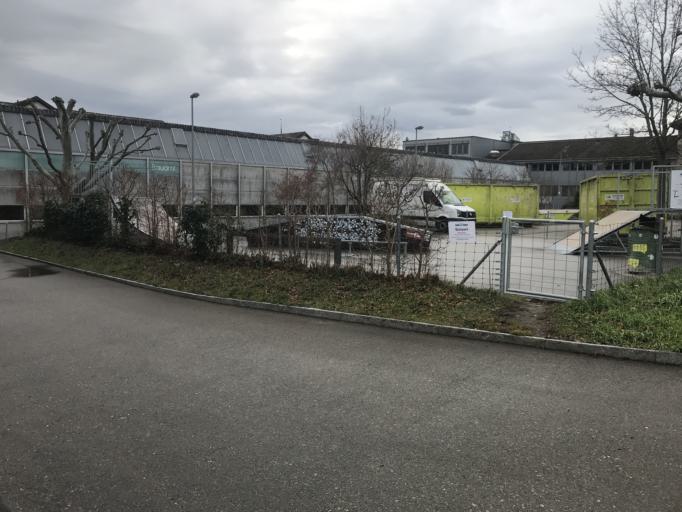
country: CH
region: Schaffhausen
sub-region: Bezirk Stein
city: Stein am Rhein
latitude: 47.6609
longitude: 8.8646
